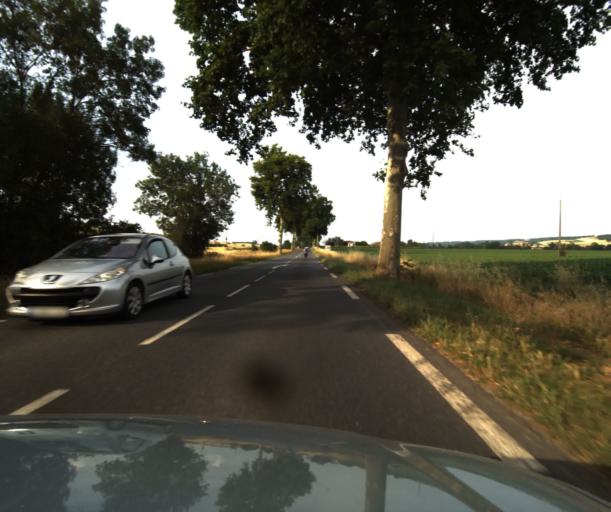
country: FR
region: Midi-Pyrenees
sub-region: Departement du Tarn-et-Garonne
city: Beaumont-de-Lomagne
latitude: 43.9073
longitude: 1.0419
